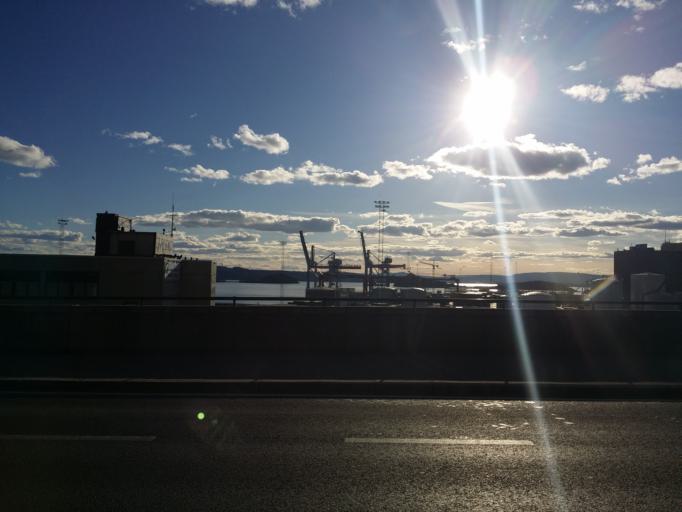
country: NO
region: Oslo
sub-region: Oslo
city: Oslo
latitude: 59.8891
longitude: 10.7647
